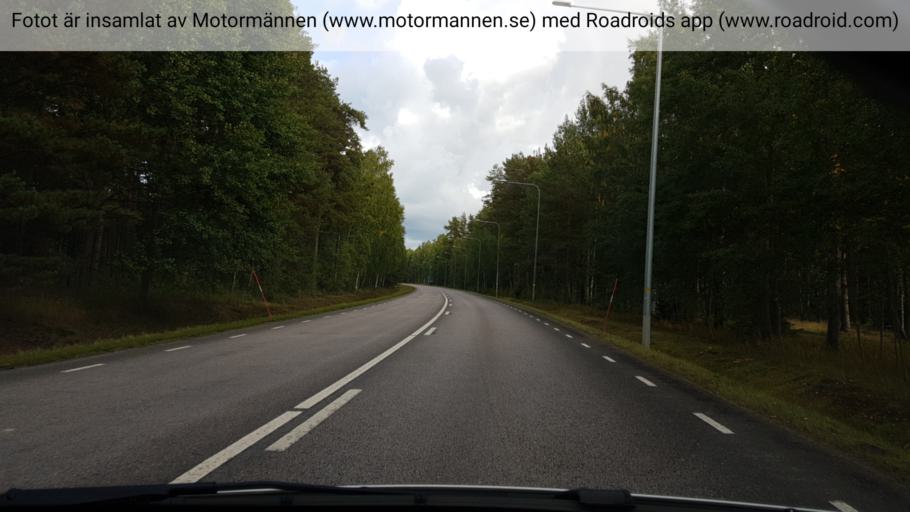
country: SE
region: Vaestra Goetaland
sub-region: Tibro Kommun
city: Tibro
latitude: 58.4106
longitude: 14.1709
